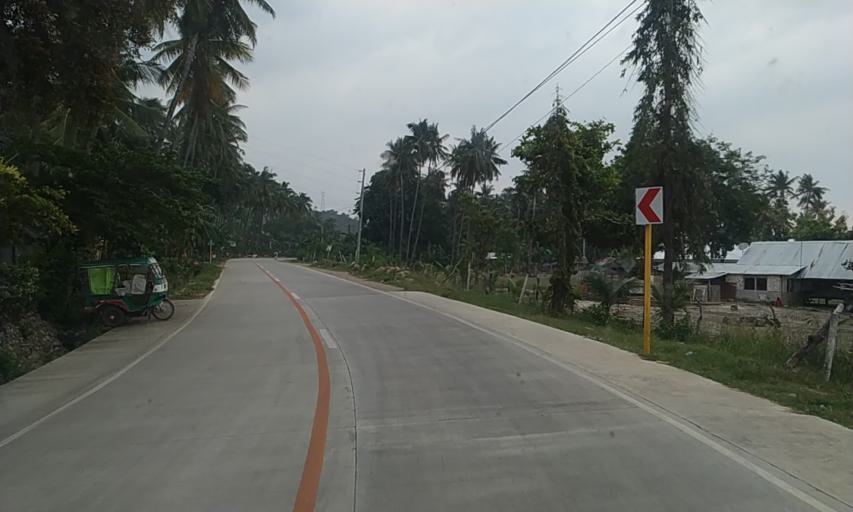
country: PH
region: Central Visayas
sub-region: Province of Negros Oriental
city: Calamba
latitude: 10.1907
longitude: 123.2939
